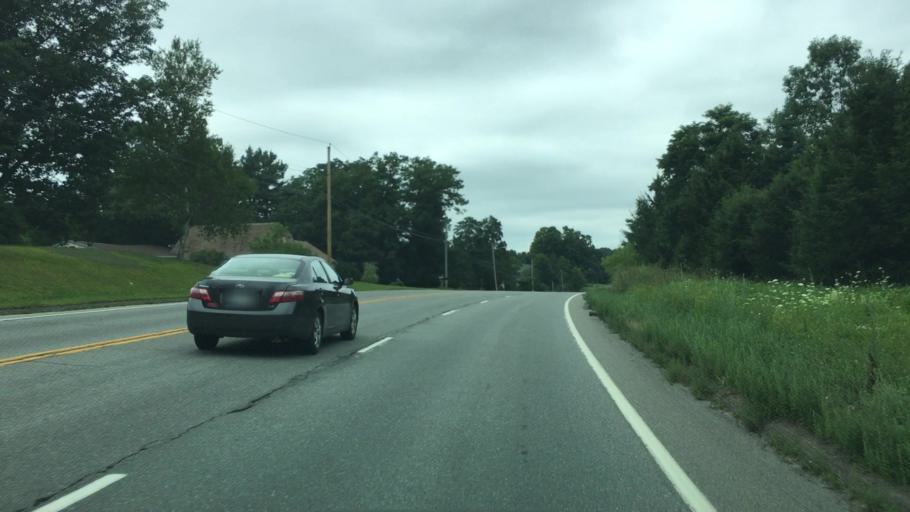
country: US
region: Maine
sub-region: Penobscot County
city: Orrington
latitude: 44.7075
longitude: -68.8468
